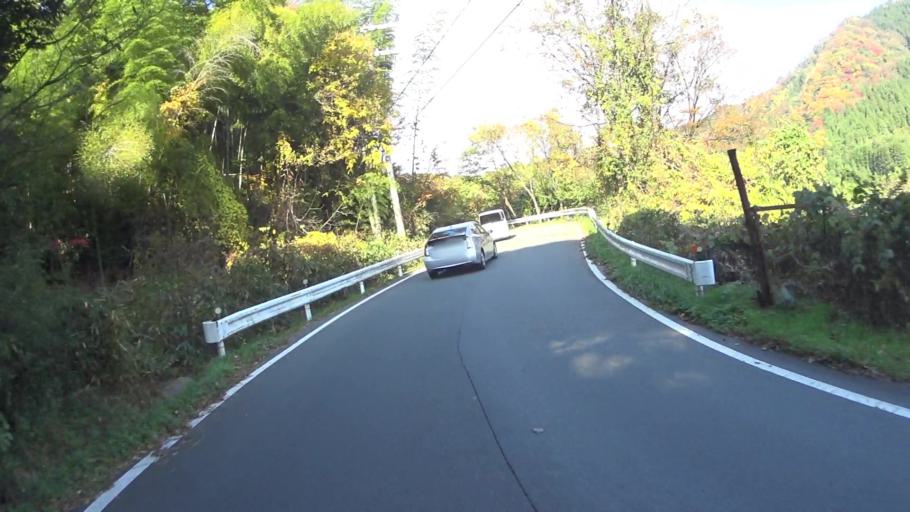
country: JP
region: Kyoto
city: Maizuru
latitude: 35.5272
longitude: 135.3921
